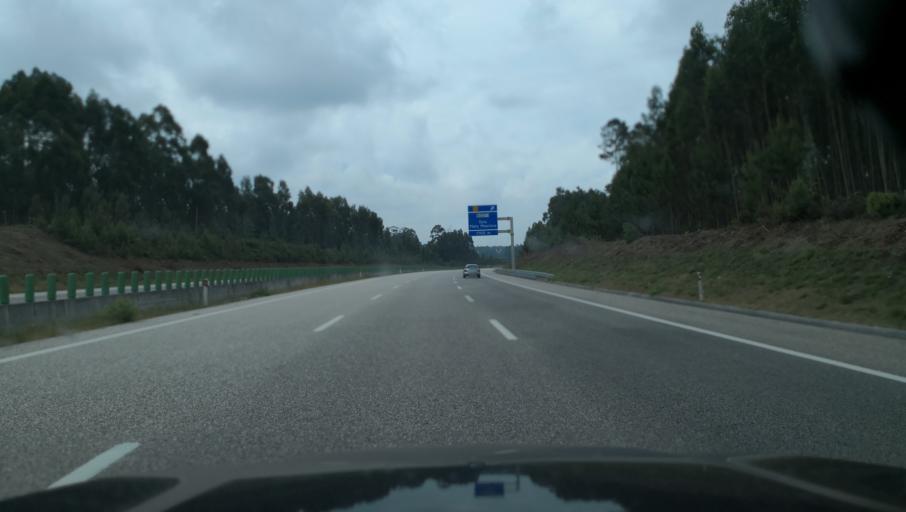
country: PT
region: Leiria
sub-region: Pombal
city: Lourical
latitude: 39.9634
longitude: -8.7764
